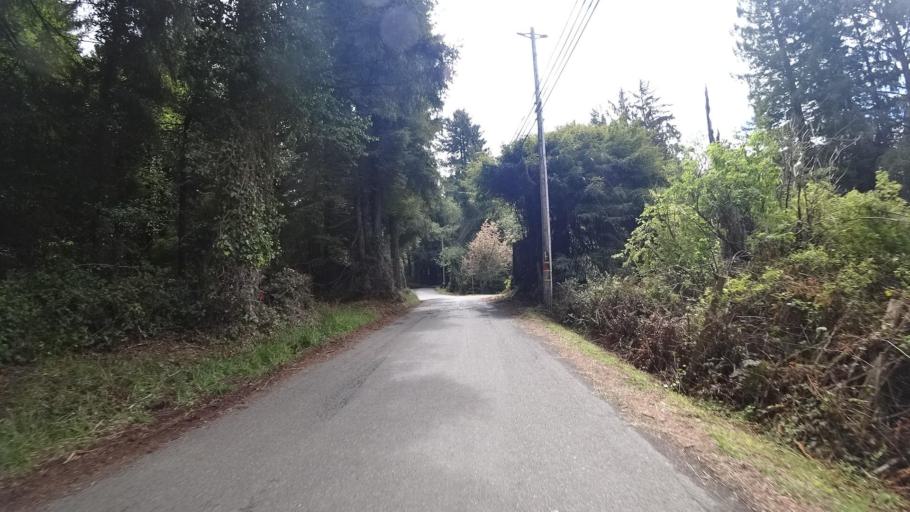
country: US
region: California
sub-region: Humboldt County
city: Bayside
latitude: 40.8563
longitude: -124.0358
